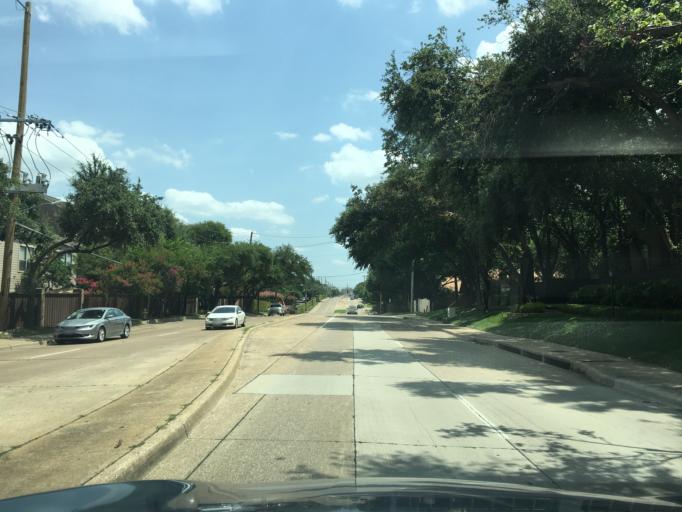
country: US
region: Texas
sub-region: Dallas County
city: Addison
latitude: 32.9428
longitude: -96.8144
